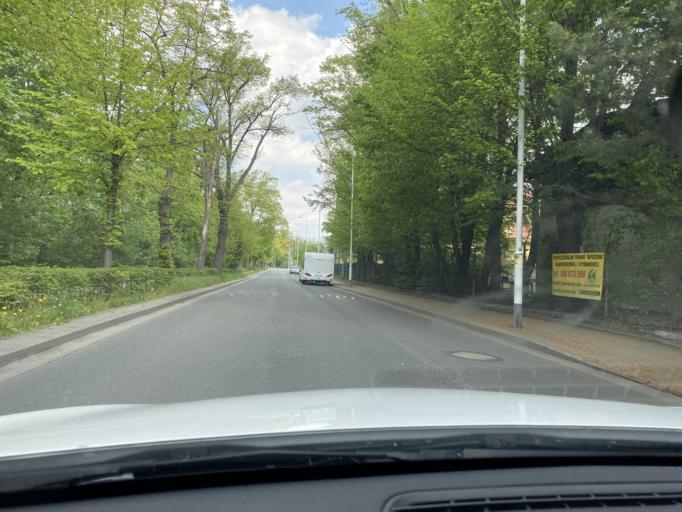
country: PL
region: Lower Silesian Voivodeship
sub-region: Powiat trzebnicki
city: Psary
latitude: 51.1457
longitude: 16.9876
